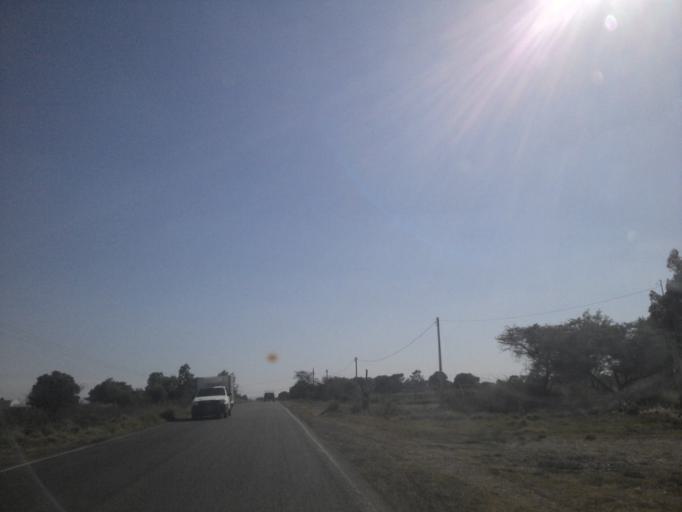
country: MX
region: Jalisco
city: Arandas
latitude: 20.7531
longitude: -102.3027
